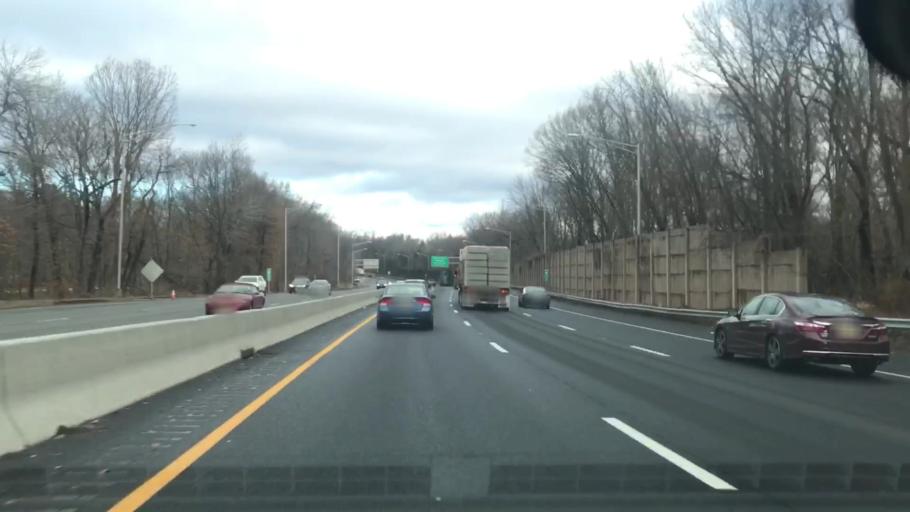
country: US
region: New Jersey
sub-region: Bergen County
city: Ho-Ho-Kus
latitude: 41.0022
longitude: -74.1015
